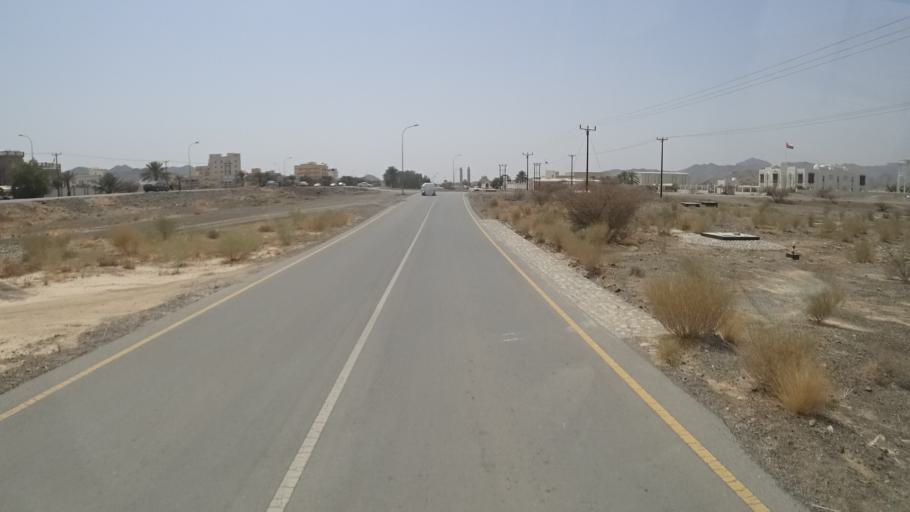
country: OM
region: Muhafazat ad Dakhiliyah
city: Bahla'
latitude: 23.0036
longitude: 57.3195
